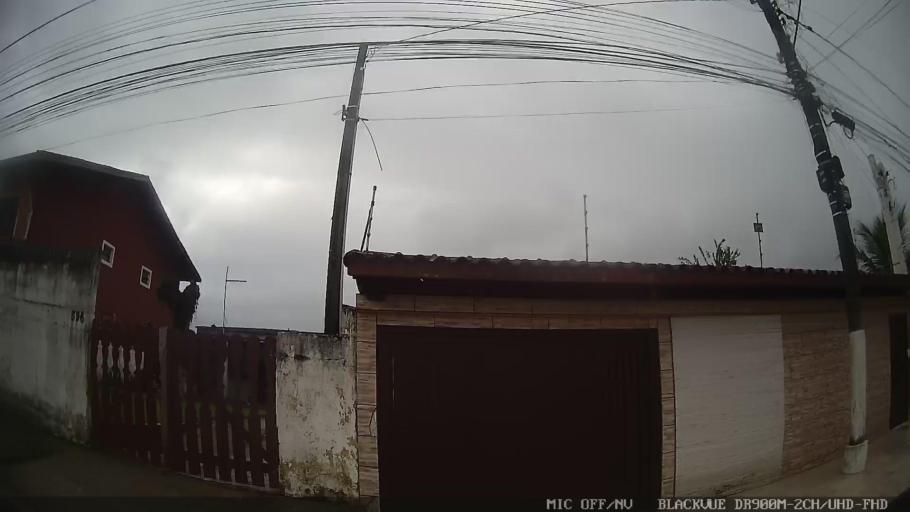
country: BR
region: Sao Paulo
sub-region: Itanhaem
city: Itanhaem
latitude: -24.1911
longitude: -46.8215
